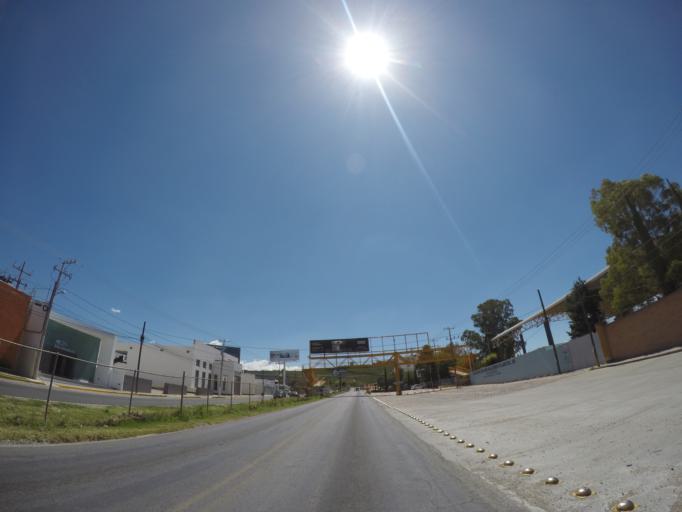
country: MX
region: San Luis Potosi
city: Escalerillas
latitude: 22.1301
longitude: -101.0369
